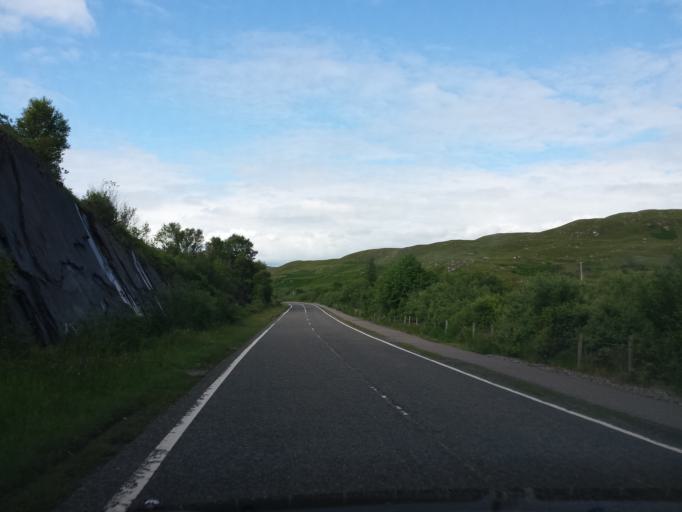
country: GB
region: Scotland
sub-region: Argyll and Bute
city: Isle Of Mull
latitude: 56.9843
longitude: -5.8268
